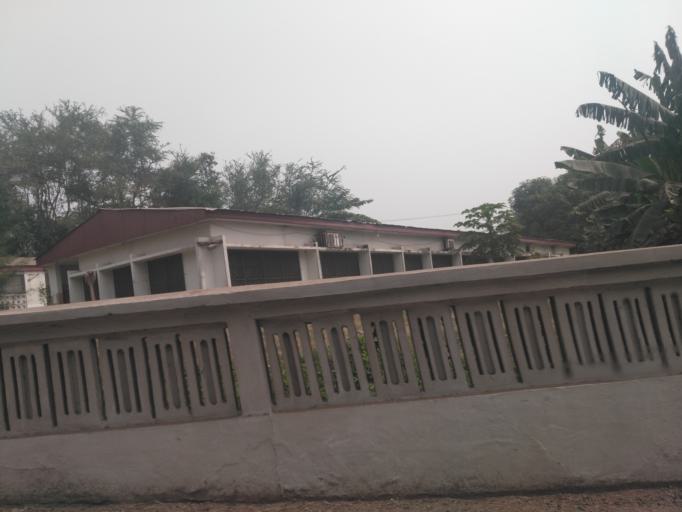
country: GH
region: Ashanti
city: Kumasi
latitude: 6.6851
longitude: -1.6234
